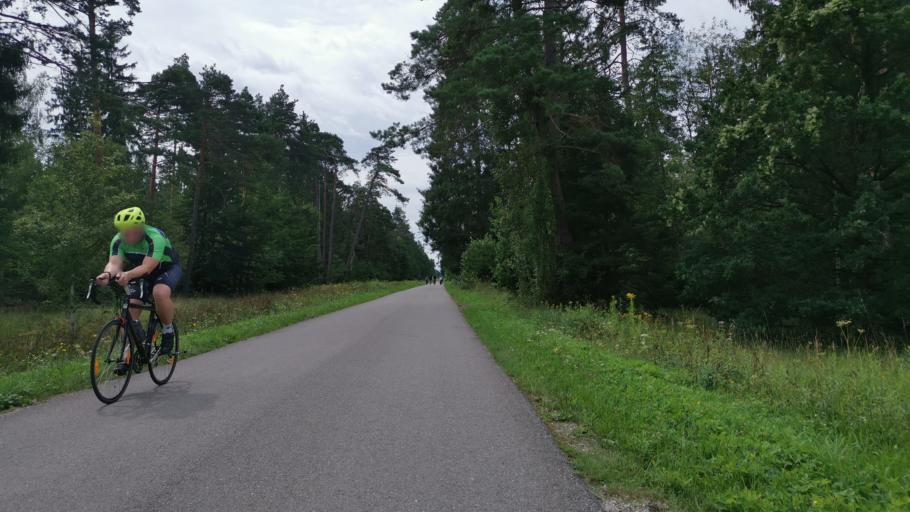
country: DE
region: Bavaria
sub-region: Upper Bavaria
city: Unterhaching
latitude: 48.0782
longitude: 11.5735
